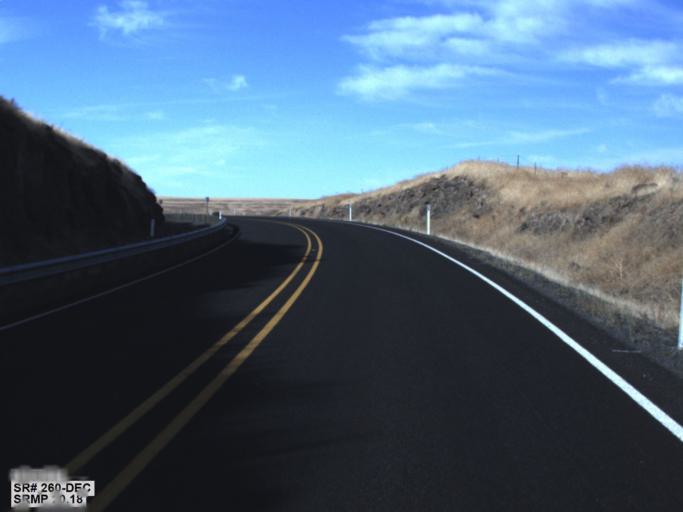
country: US
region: Washington
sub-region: Franklin County
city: Connell
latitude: 46.6320
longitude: -118.6399
